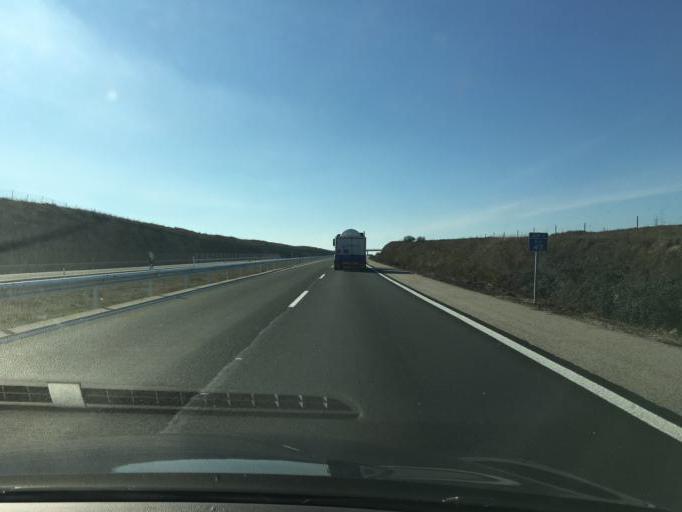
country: ES
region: Castille and Leon
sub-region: Provincia de Burgos
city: Zuneda
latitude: 42.5908
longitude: -3.2331
